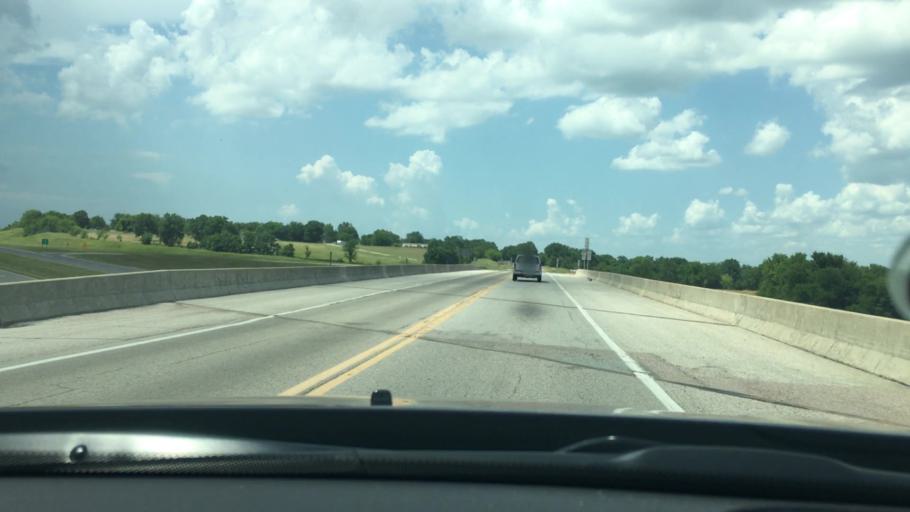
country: US
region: Oklahoma
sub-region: Pontotoc County
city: Ada
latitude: 34.7256
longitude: -96.6348
